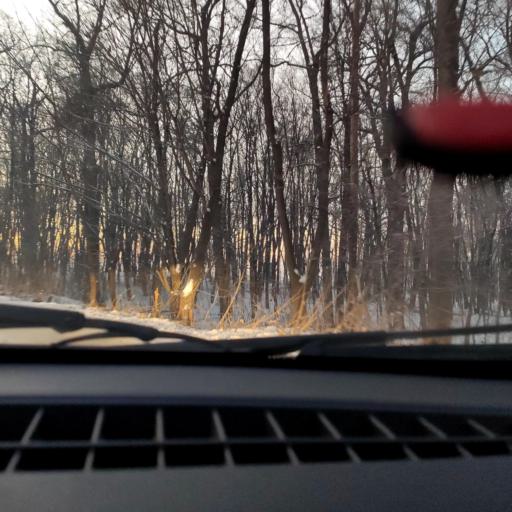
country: RU
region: Bashkortostan
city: Ufa
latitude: 54.7565
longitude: 55.9836
